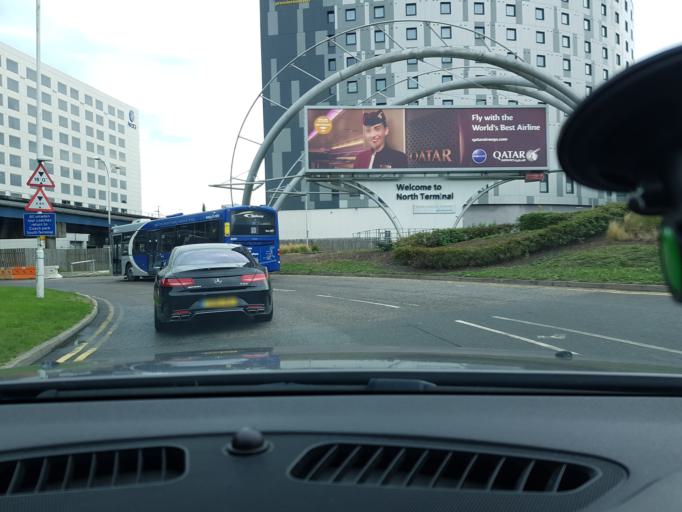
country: GB
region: England
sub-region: Surrey
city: Horley
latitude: 51.1619
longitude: -0.1730
